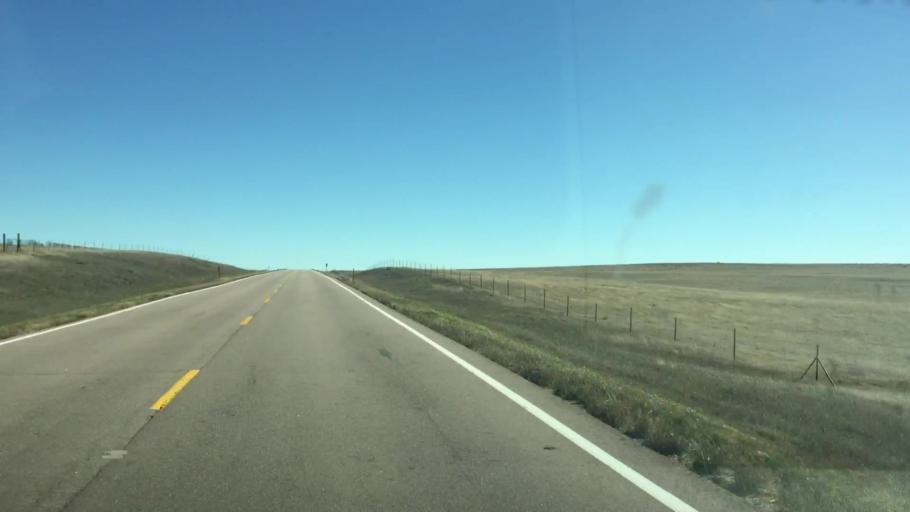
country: US
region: Colorado
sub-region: Lincoln County
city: Limon
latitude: 39.2751
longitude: -104.0049
